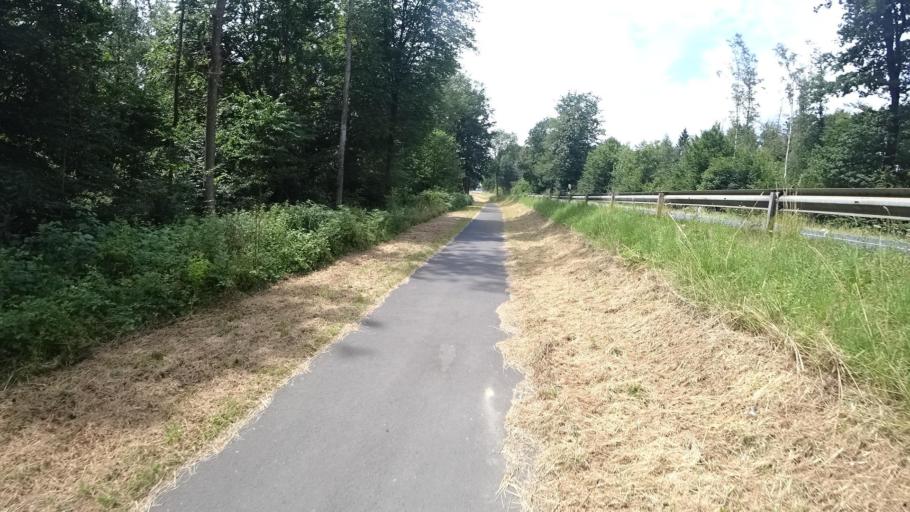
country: DE
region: Rheinland-Pfalz
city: Oberirsen
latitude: 50.7125
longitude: 7.5683
